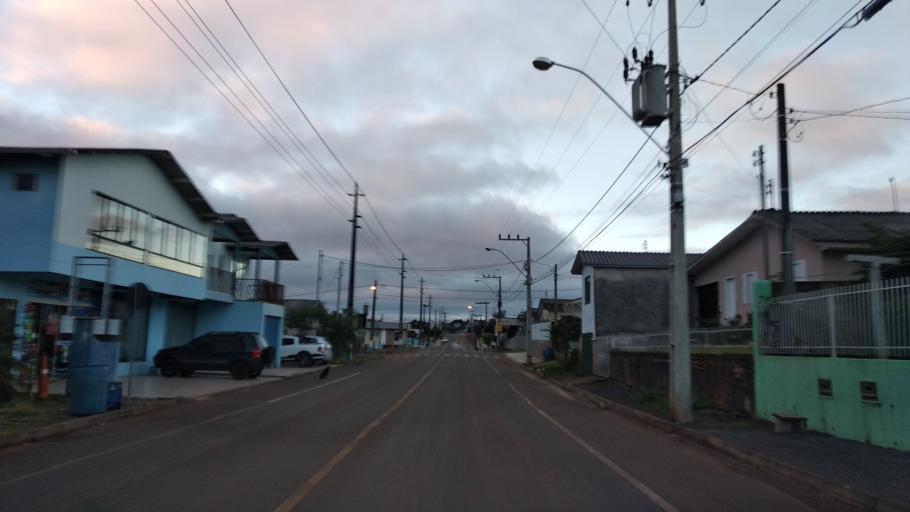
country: BR
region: Santa Catarina
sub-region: Campos Novos
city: Campos Novos
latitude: -27.3855
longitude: -51.2110
